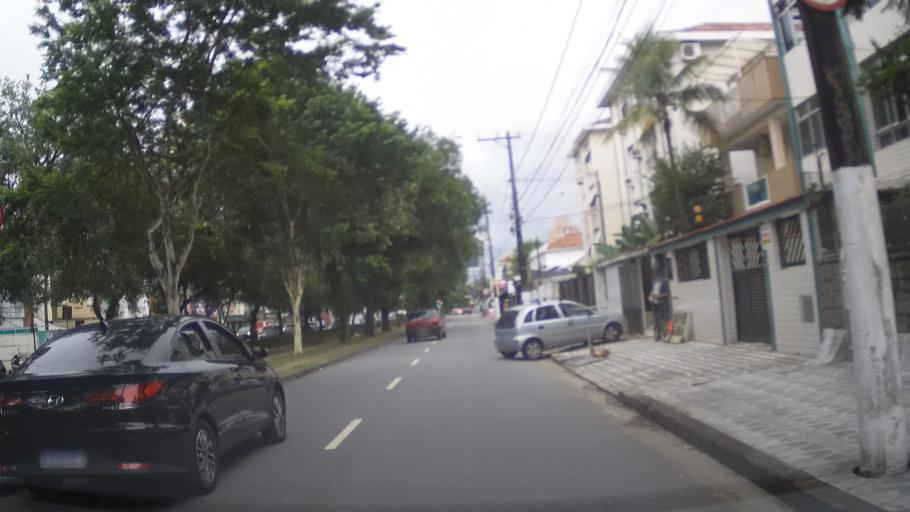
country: BR
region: Sao Paulo
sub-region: Santos
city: Santos
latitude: -23.9663
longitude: -46.3195
